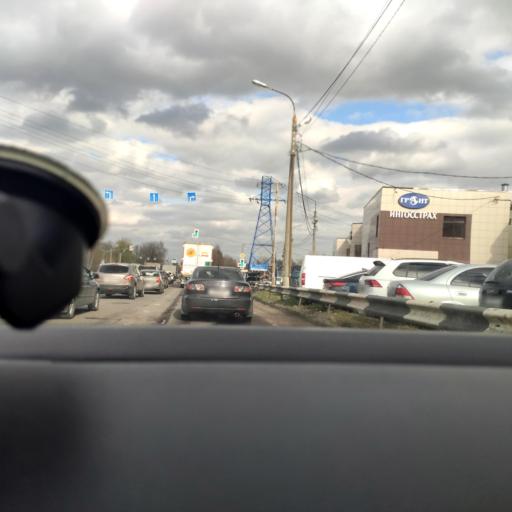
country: RU
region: Moskovskaya
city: Chornaya
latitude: 55.7505
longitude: 38.0543
